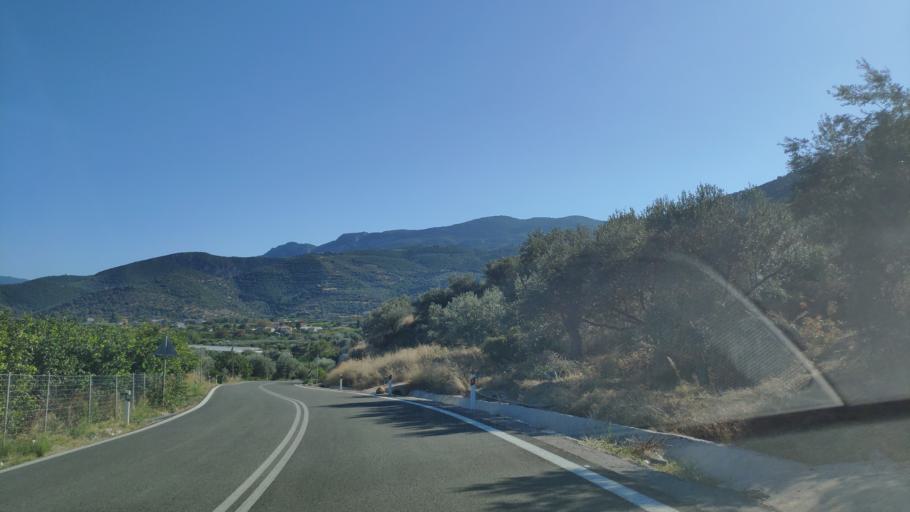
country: GR
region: Peloponnese
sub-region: Nomos Argolidos
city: Didyma
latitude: 37.5477
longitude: 23.2832
